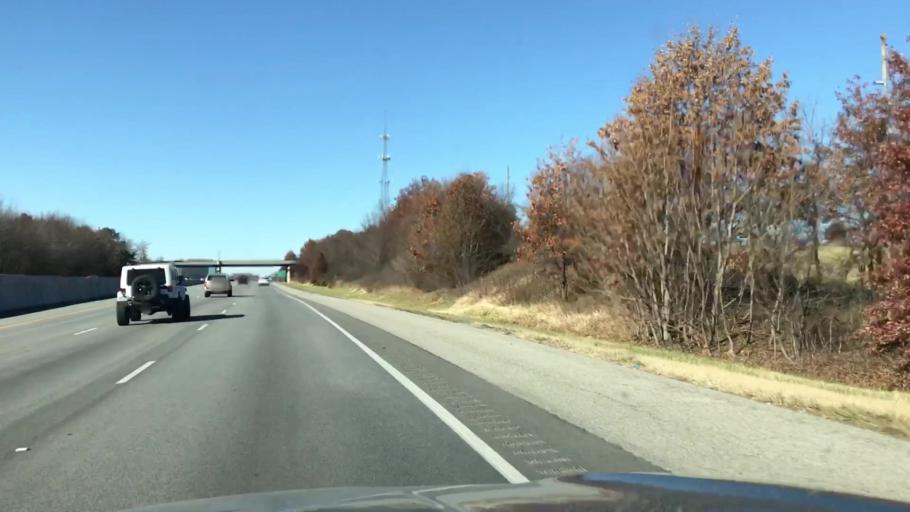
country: US
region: Arkansas
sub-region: Benton County
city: Lowell
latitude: 36.2962
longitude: -94.1680
